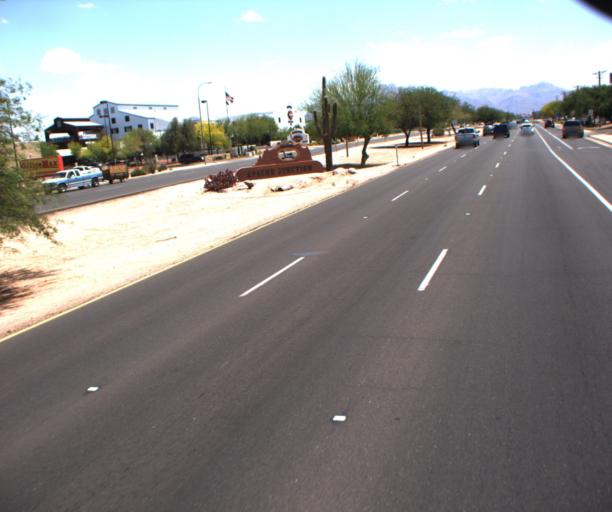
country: US
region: Arizona
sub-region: Pinal County
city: Apache Junction
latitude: 33.4151
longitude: -111.5800
